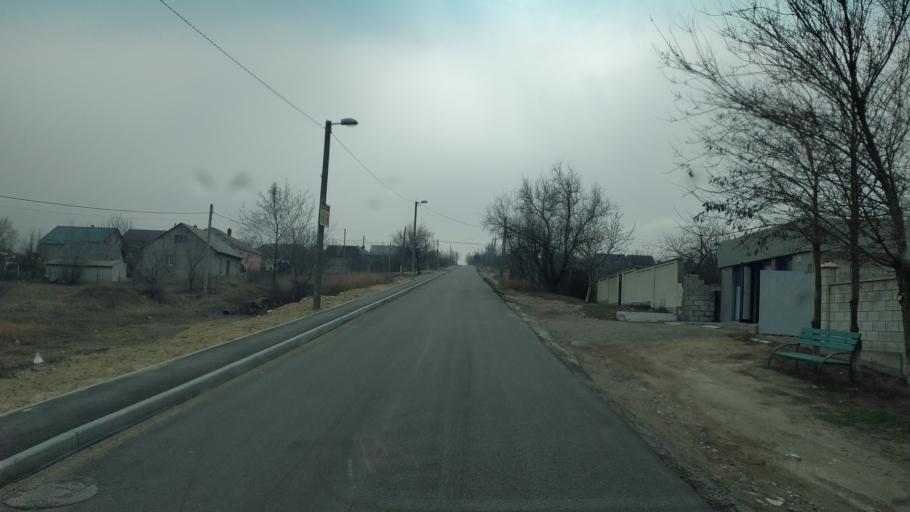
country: MD
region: Chisinau
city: Singera
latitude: 46.9117
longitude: 28.9871
